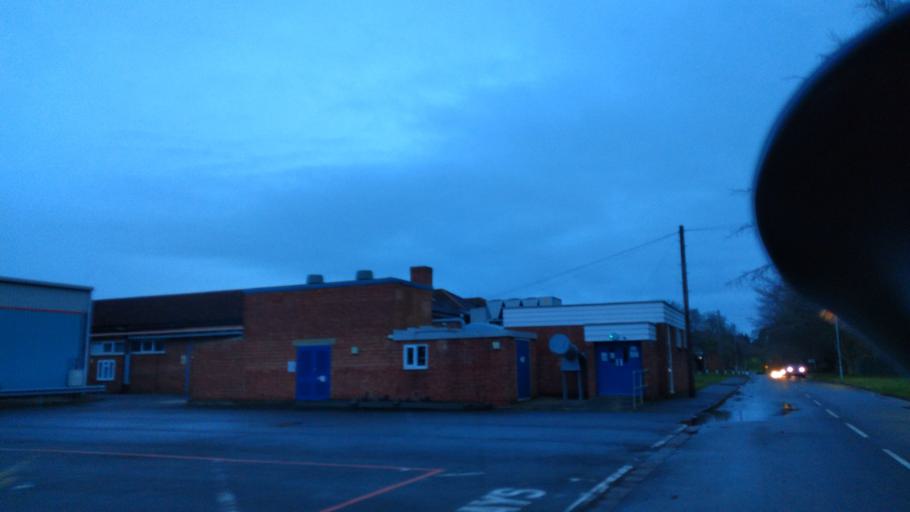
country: GB
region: England
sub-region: Oxfordshire
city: Shrivenham
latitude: 51.6044
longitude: -1.6348
